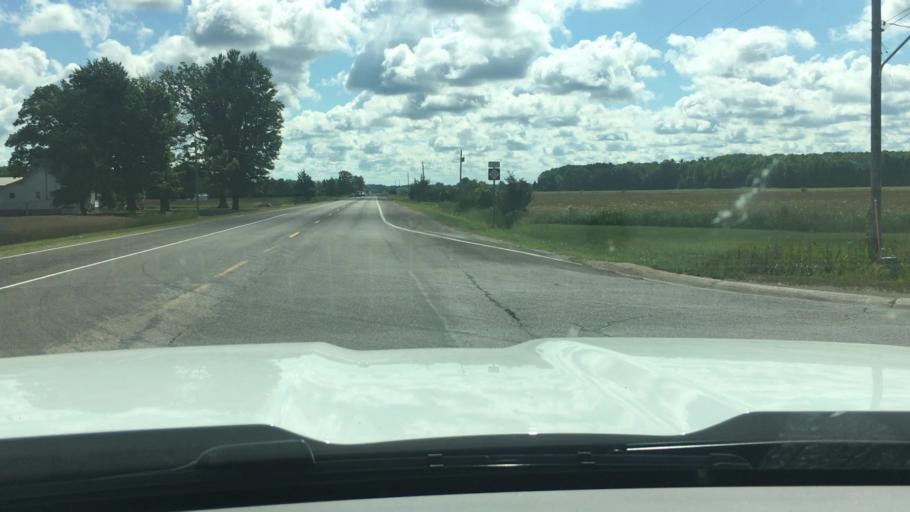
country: US
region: Michigan
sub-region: Clinton County
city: Ovid
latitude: 43.1760
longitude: -84.3882
